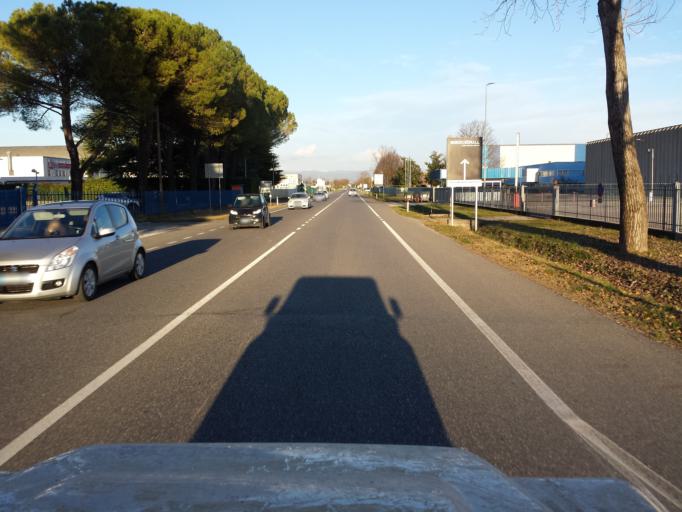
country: IT
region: Friuli Venezia Giulia
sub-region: Provincia di Gorizia
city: Villesse
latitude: 45.8715
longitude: 13.4520
